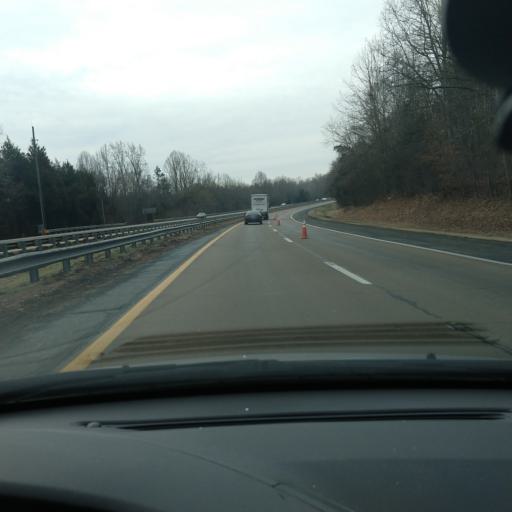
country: US
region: North Carolina
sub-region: Forsyth County
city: Winston-Salem
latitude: 36.0298
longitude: -80.2367
